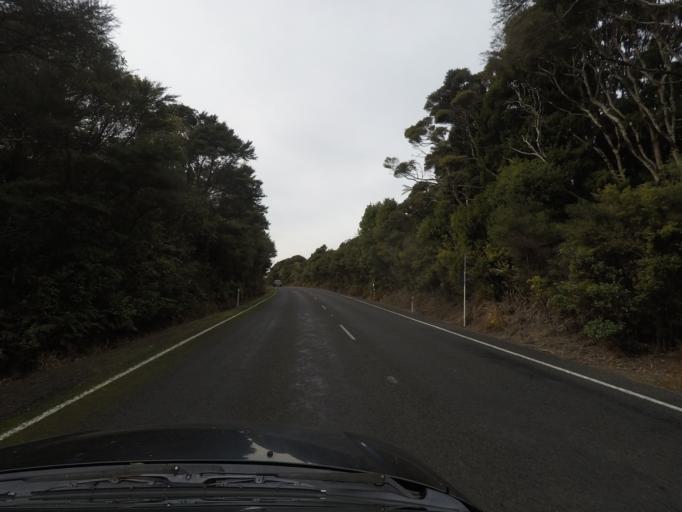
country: NZ
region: Auckland
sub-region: Auckland
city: Titirangi
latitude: -36.9439
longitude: 174.5479
